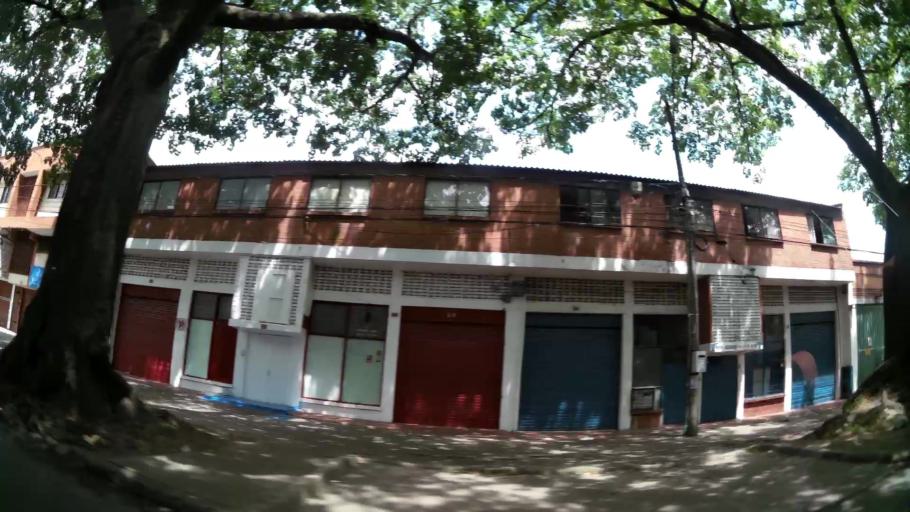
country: CO
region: Valle del Cauca
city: Cali
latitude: 3.4558
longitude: -76.5231
